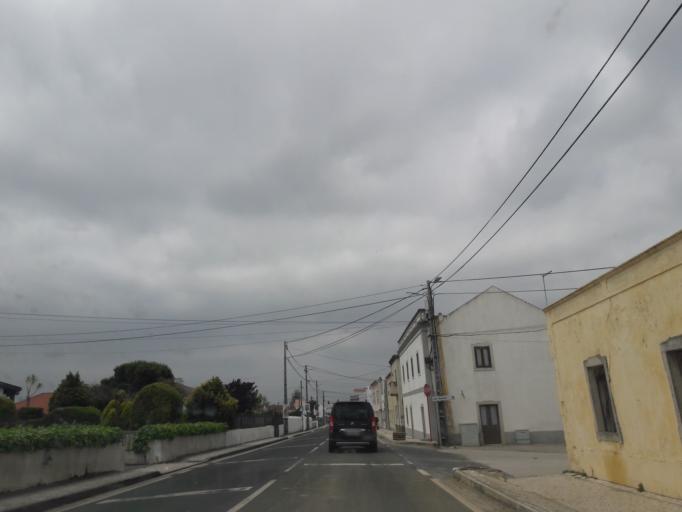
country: PT
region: Leiria
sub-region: Peniche
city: Atouguia da Baleia
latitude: 39.3326
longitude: -9.2676
